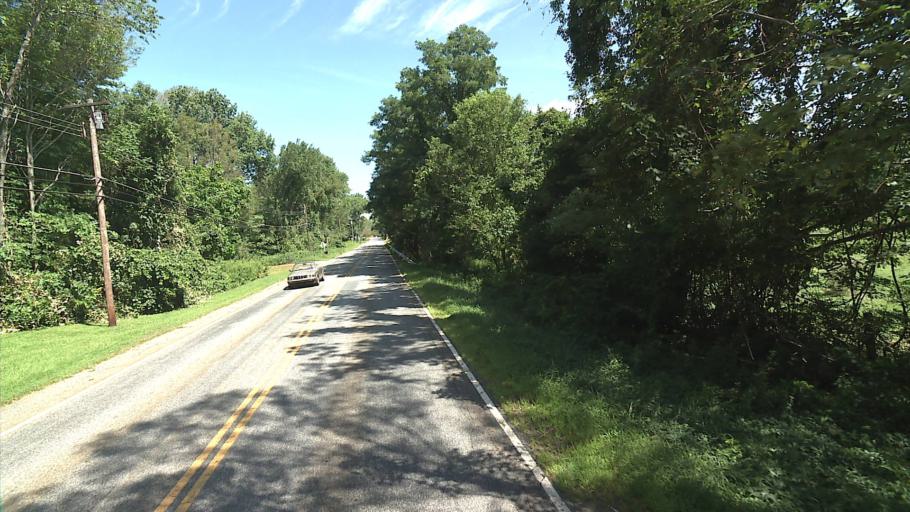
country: US
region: Connecticut
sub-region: Windham County
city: South Woodstock
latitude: 41.8447
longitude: -72.0157
